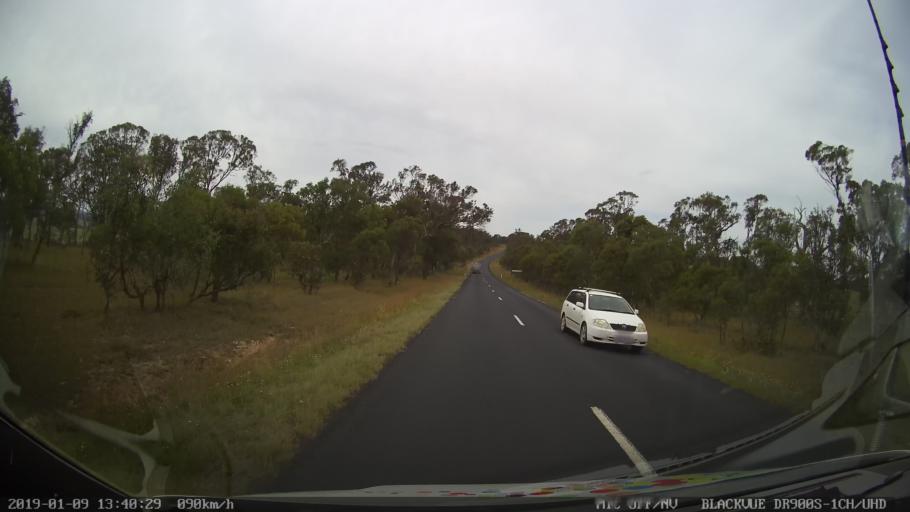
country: AU
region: New South Wales
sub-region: Armidale Dumaresq
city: Enmore
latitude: -30.5064
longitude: 152.1356
